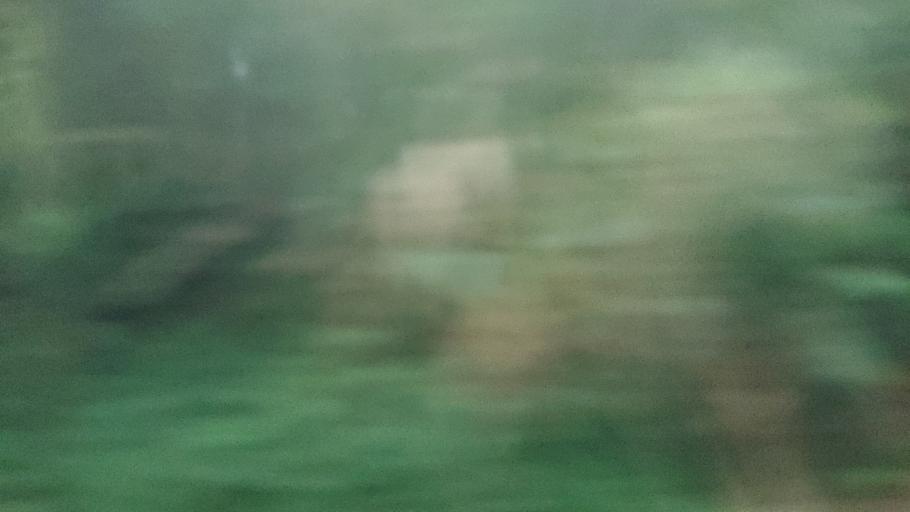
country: TW
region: Taiwan
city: Lugu
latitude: 23.5036
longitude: 120.7021
